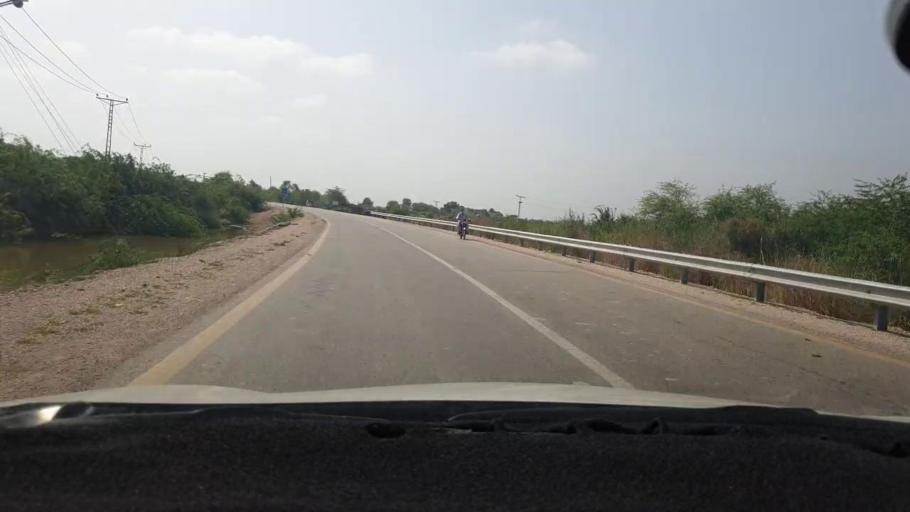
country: PK
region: Sindh
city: Mirpur Khas
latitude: 25.7482
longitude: 69.0844
